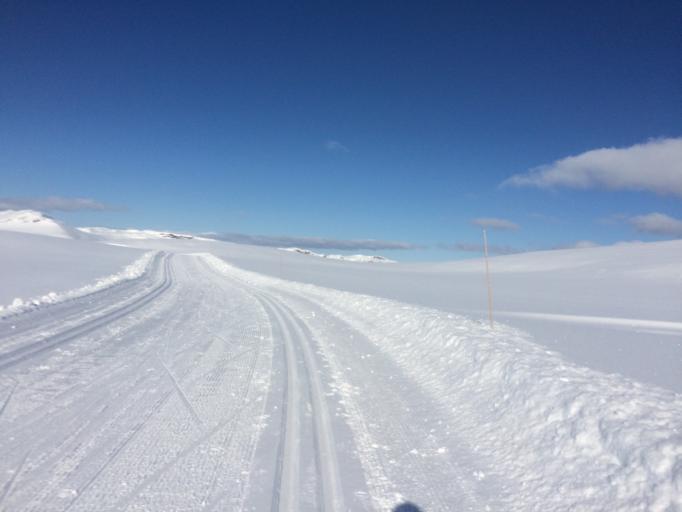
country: NO
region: Oppland
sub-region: Ringebu
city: Ringebu
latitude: 61.3549
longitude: 10.0871
